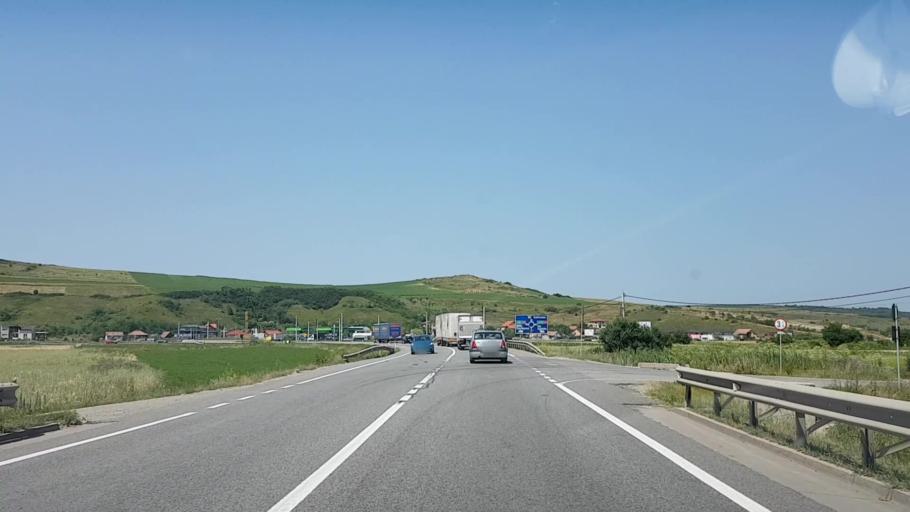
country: RO
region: Cluj
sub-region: Comuna Apahida
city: Sannicoara
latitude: 46.7946
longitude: 23.7177
